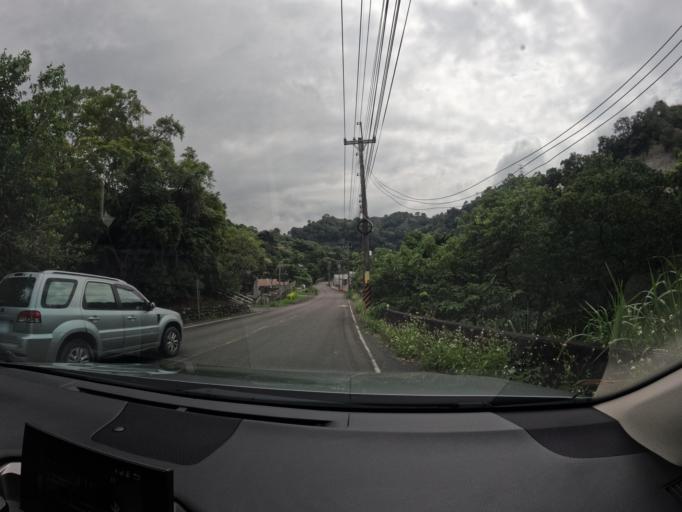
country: TW
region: Taiwan
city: Fengyuan
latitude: 24.3485
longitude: 120.8714
